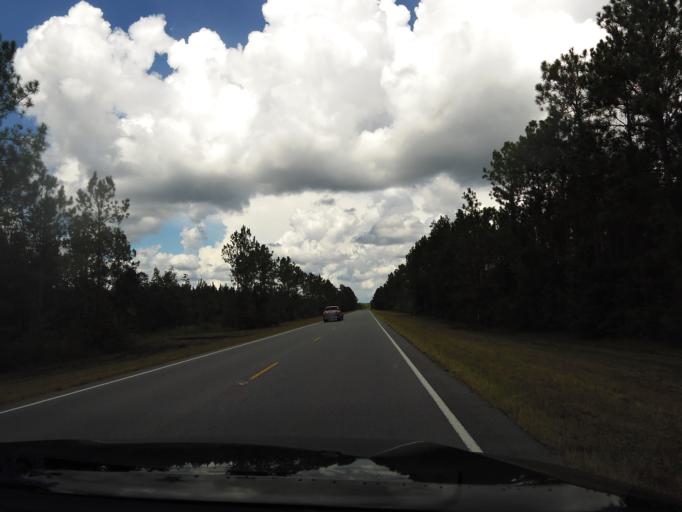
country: US
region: Georgia
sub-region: Charlton County
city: Folkston
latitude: 30.9162
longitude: -82.0196
